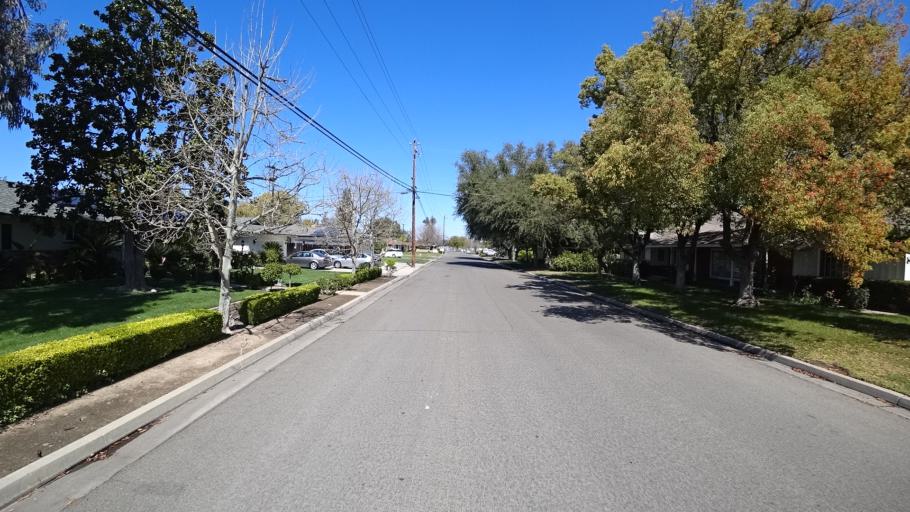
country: US
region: California
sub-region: Fresno County
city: Fresno
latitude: 36.8139
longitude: -119.8129
